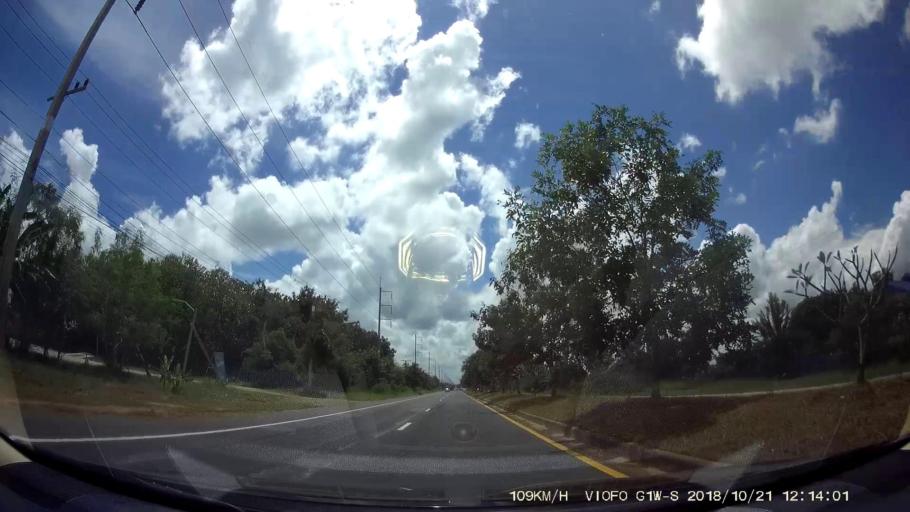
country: TH
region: Chaiyaphum
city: Chatturat
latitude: 15.3839
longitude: 101.8372
